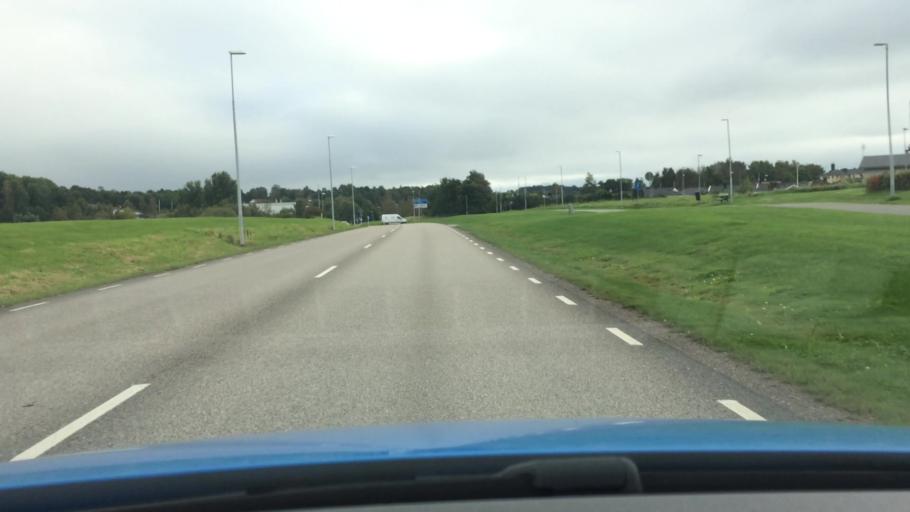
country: SE
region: Halland
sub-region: Kungsbacka Kommun
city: Kungsbacka
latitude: 57.4953
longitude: 12.0912
